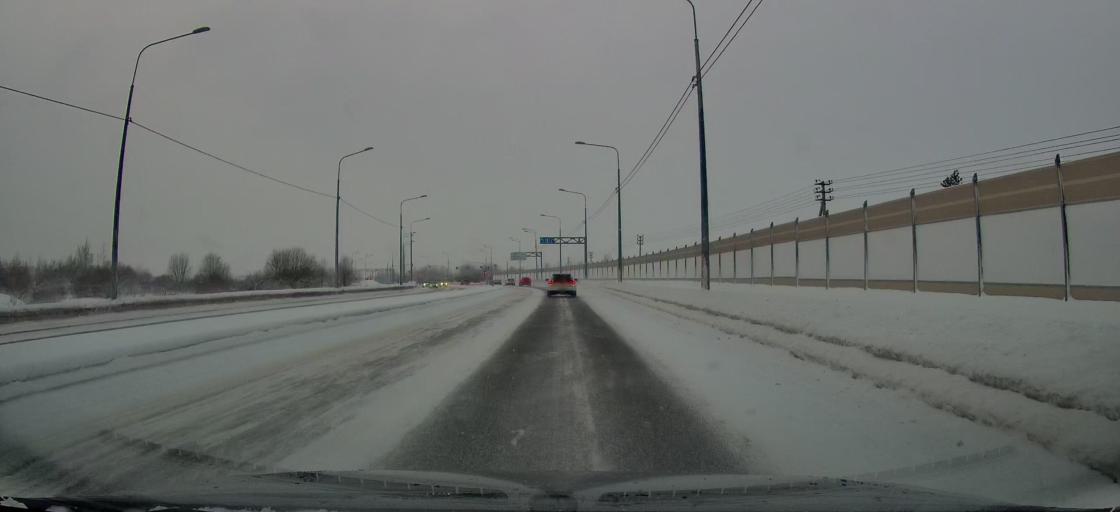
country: RU
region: St.-Petersburg
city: Krasnoye Selo
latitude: 59.7522
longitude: 30.0944
